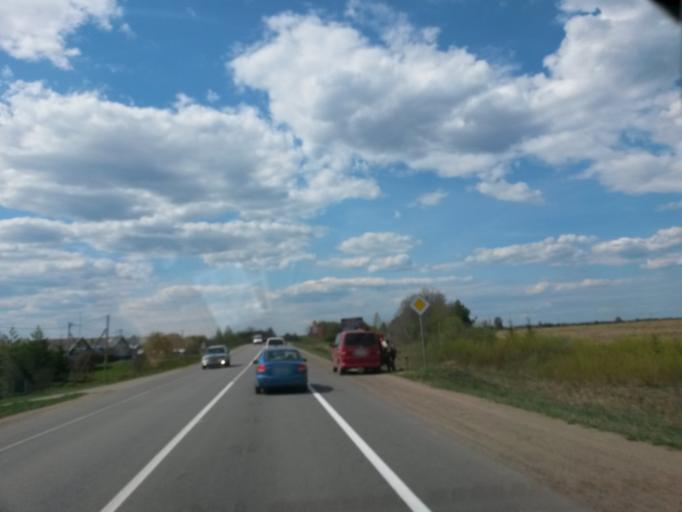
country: RU
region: Jaroslavl
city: Bol'shoye Selo
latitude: 57.7250
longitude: 38.9279
